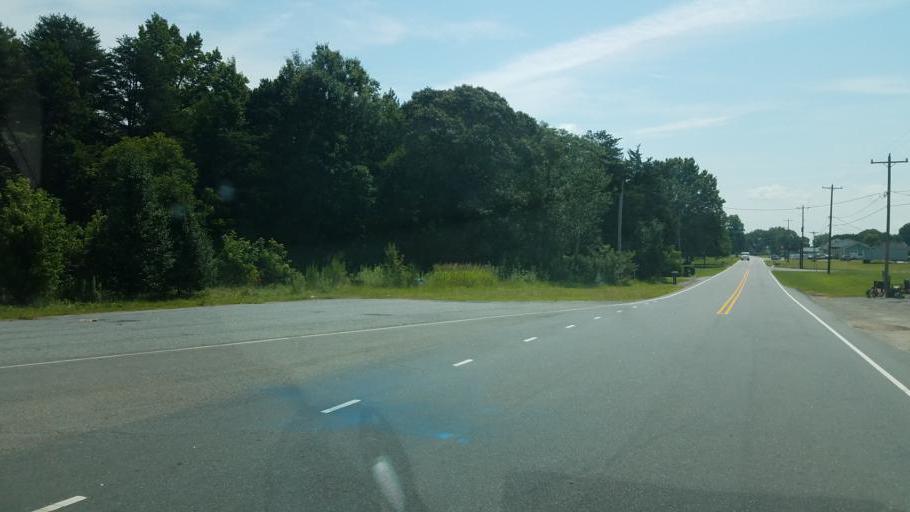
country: US
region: North Carolina
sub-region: Gaston County
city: Cherryville
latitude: 35.5109
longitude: -81.4613
